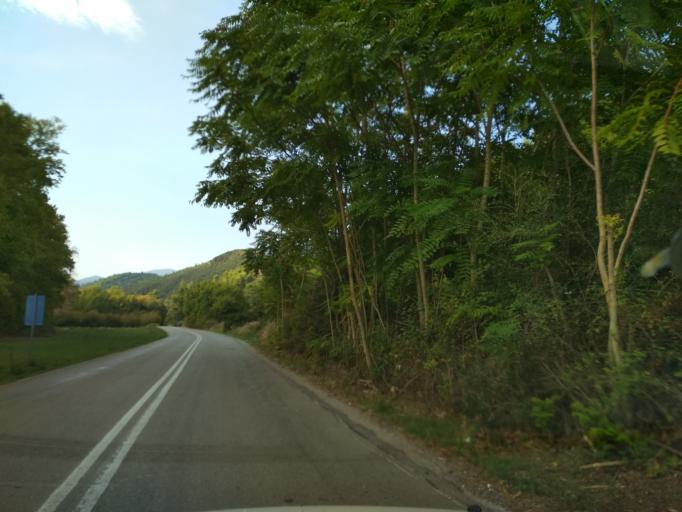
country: GR
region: Central Greece
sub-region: Nomos Evvoias
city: Mantoudi
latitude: 38.7820
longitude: 23.4702
